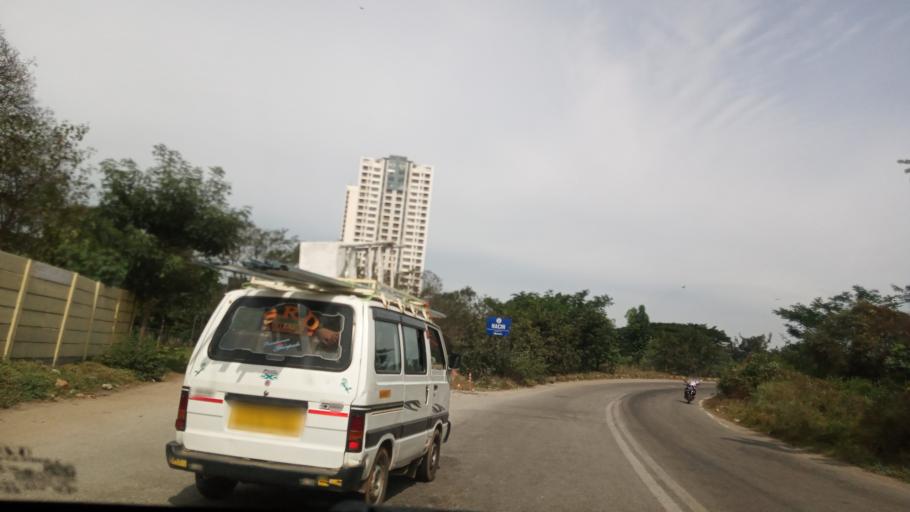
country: IN
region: Karnataka
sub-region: Bangalore Urban
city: Yelahanka
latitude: 13.0430
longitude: 77.5393
